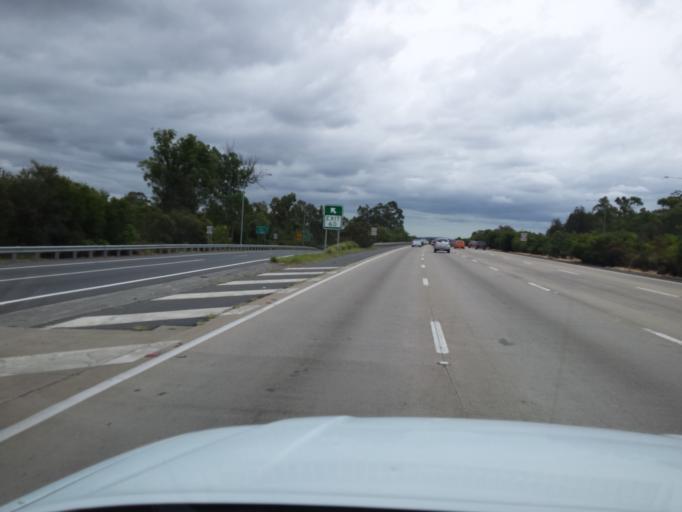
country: AU
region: Queensland
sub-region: Gold Coast
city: Upper Coomera
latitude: -27.9125
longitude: 153.3188
